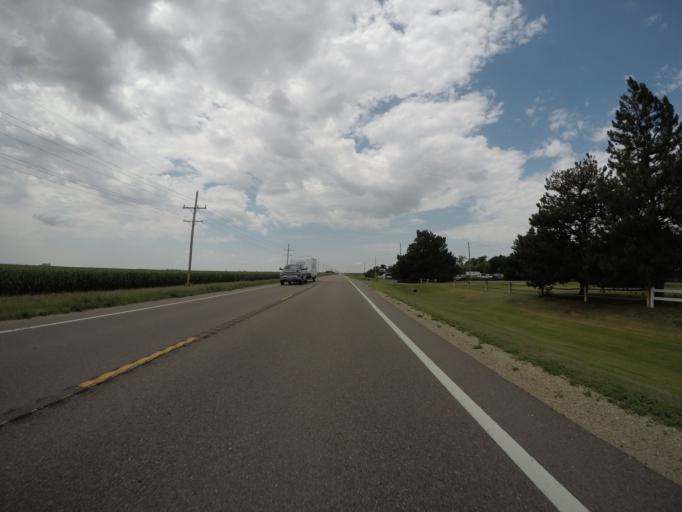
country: US
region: Kansas
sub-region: Thomas County
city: Colby
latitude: 39.3944
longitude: -100.9721
